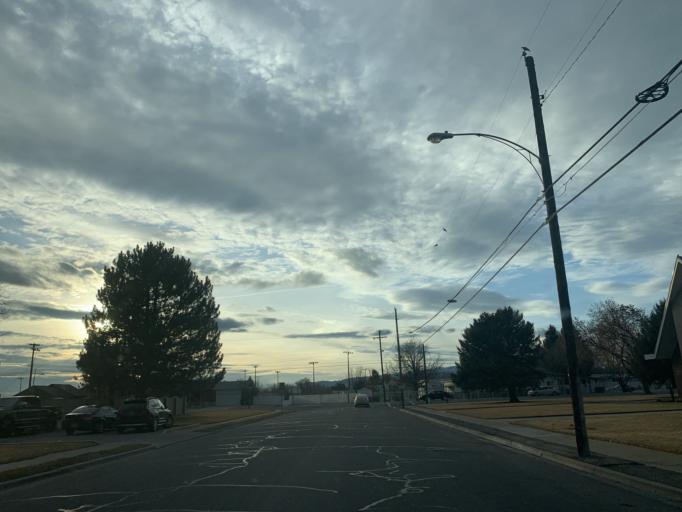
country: US
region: Utah
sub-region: Utah County
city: Provo
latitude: 40.2203
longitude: -111.6768
